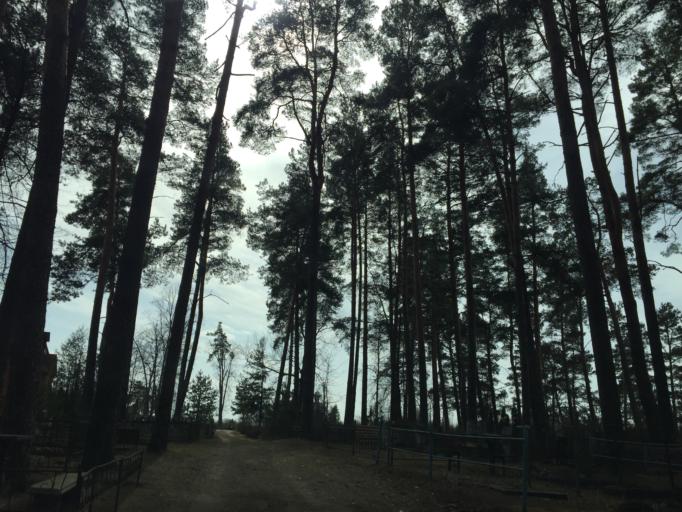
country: LV
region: Daugavpils
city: Daugavpils
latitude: 55.9010
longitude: 26.4796
